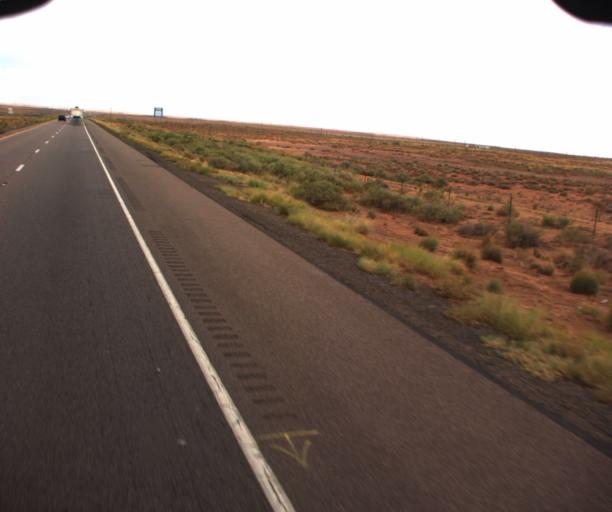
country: US
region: Arizona
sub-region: Coconino County
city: LeChee
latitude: 35.0766
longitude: -110.8662
